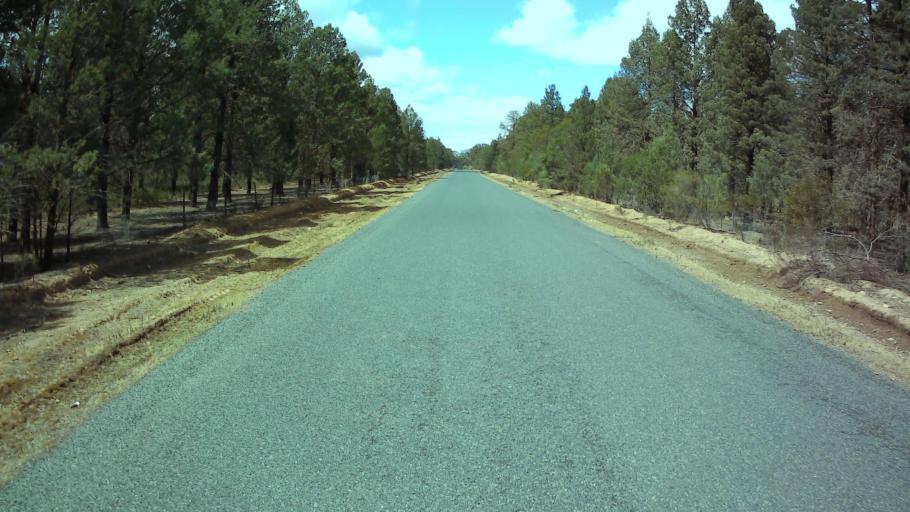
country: AU
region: New South Wales
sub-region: Weddin
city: Grenfell
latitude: -33.9006
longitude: 147.9208
